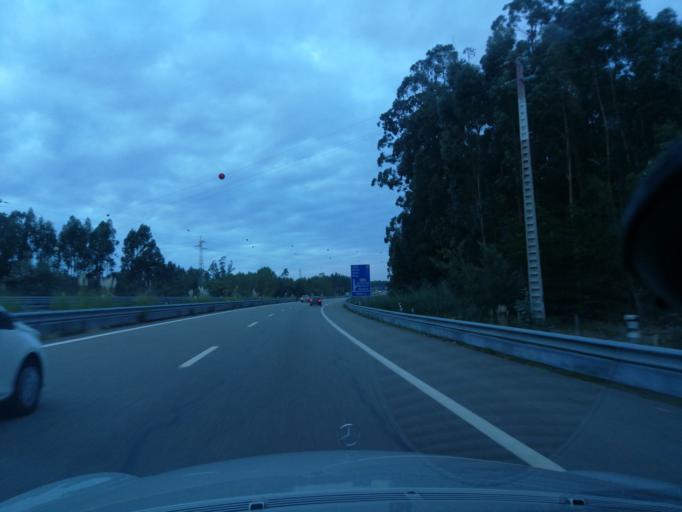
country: PT
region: Aveiro
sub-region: Estarreja
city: Beduido
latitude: 40.7743
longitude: -8.5605
